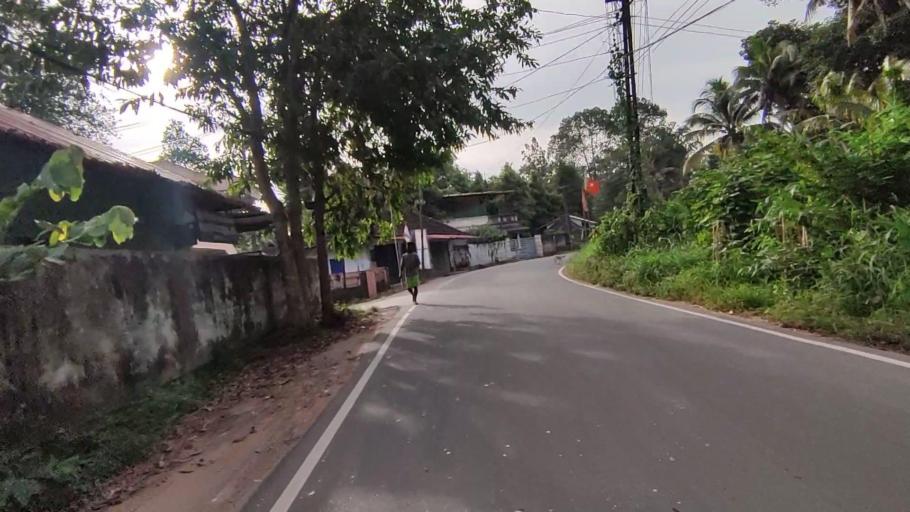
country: IN
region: Kerala
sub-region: Kottayam
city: Kottayam
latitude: 9.6023
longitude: 76.5024
